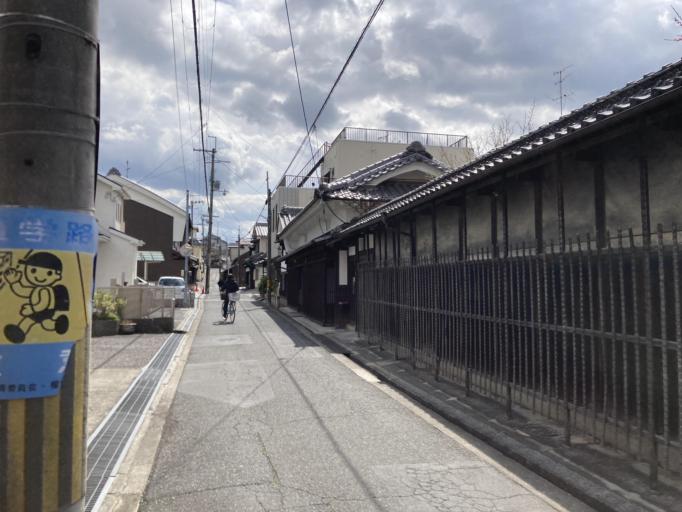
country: JP
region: Nara
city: Kashihara-shi
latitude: 34.5037
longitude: 135.7962
